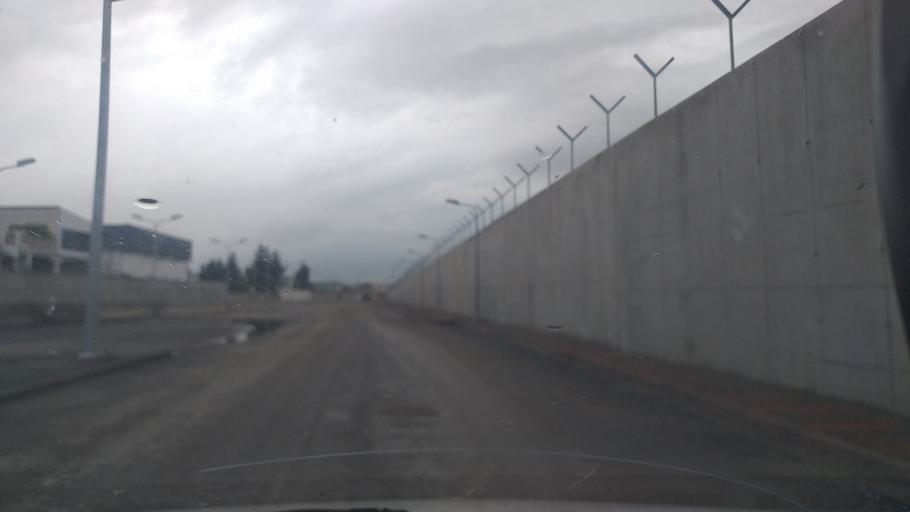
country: TN
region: Ariana
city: Ariana
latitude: 36.8532
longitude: 10.2125
